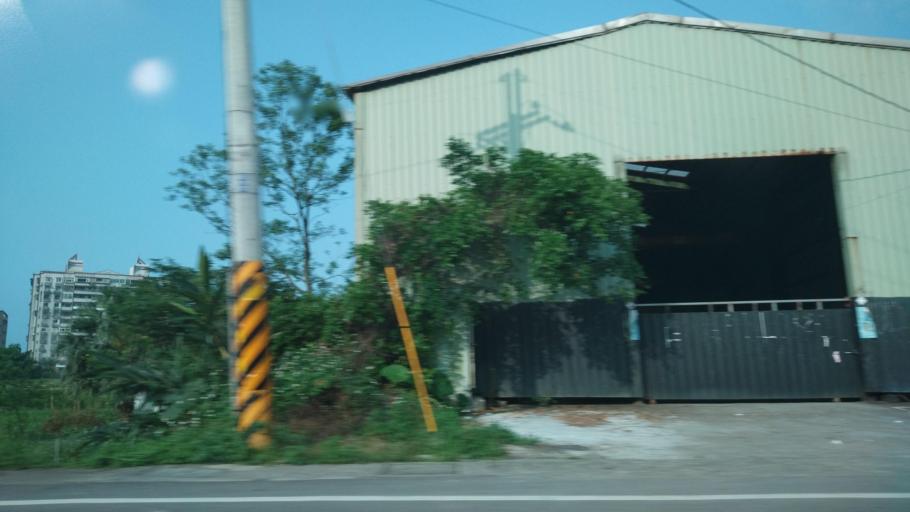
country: TW
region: Taiwan
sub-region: Keelung
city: Keelung
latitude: 25.2230
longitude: 121.6315
